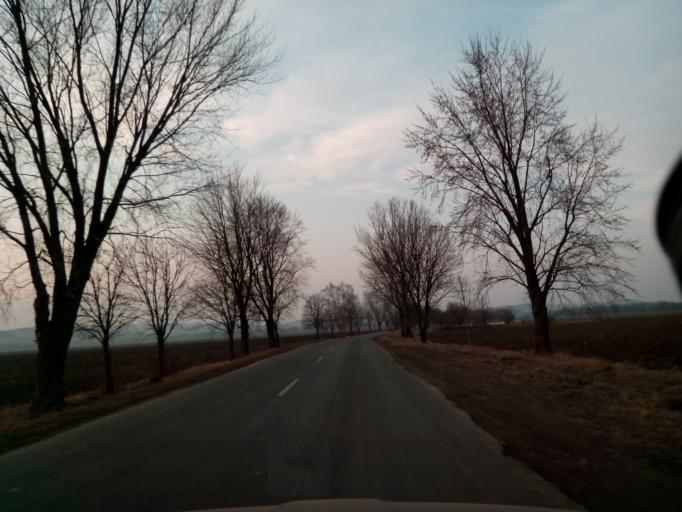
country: HU
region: Borsod-Abauj-Zemplen
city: Gonc
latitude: 48.4830
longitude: 21.2549
